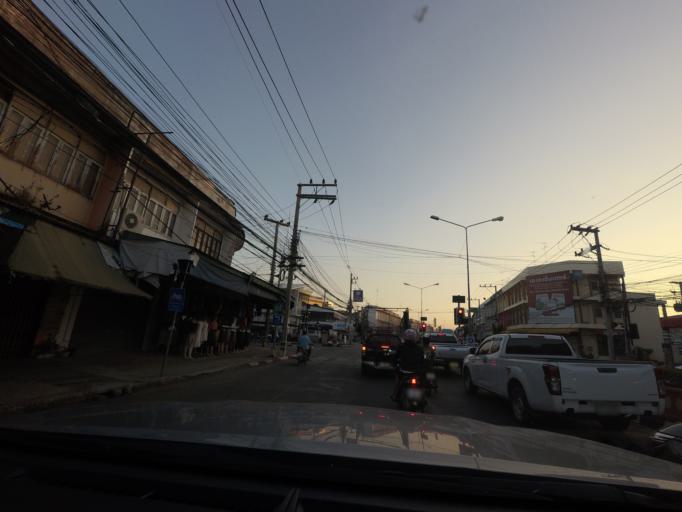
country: TH
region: Sukhothai
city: Sukhothai
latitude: 17.0123
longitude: 99.8208
